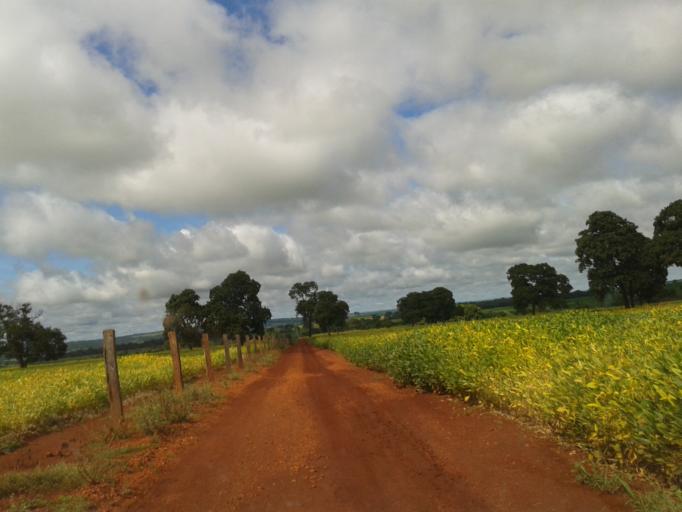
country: BR
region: Minas Gerais
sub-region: Santa Vitoria
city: Santa Vitoria
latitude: -18.7630
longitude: -49.8505
